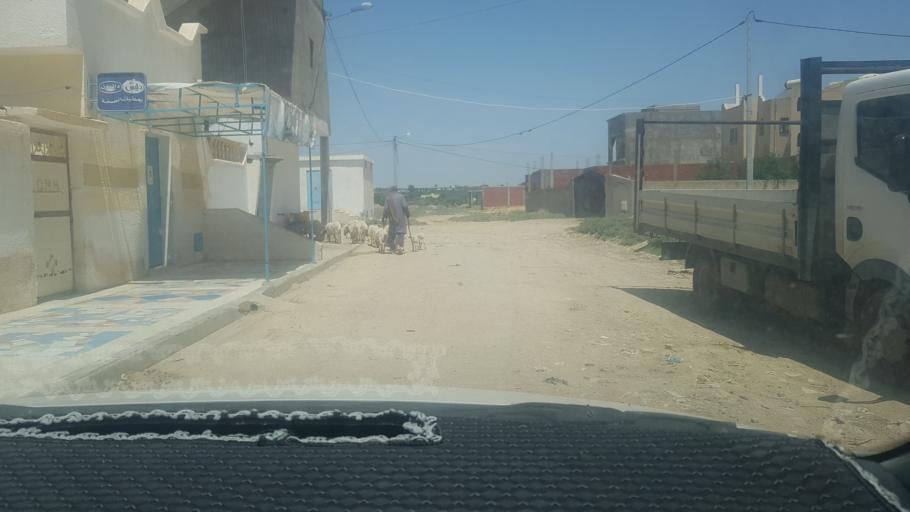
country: TN
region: Al Qayrawan
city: Kairouan
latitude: 35.6211
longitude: 9.9285
